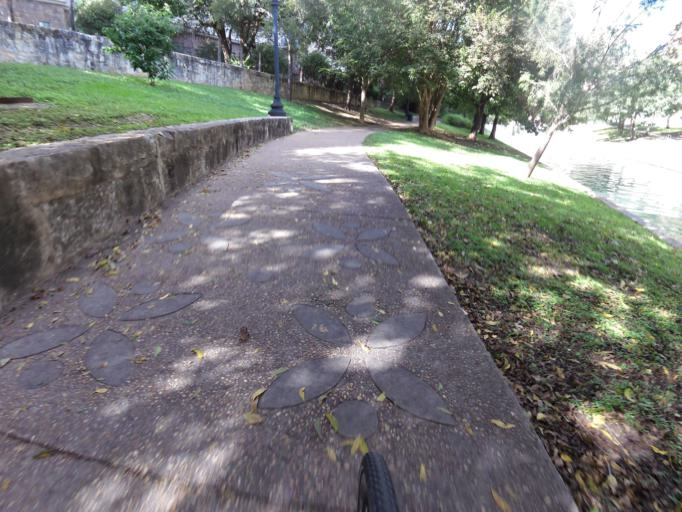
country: US
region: Texas
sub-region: Bexar County
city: San Antonio
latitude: 29.4201
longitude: -98.4925
